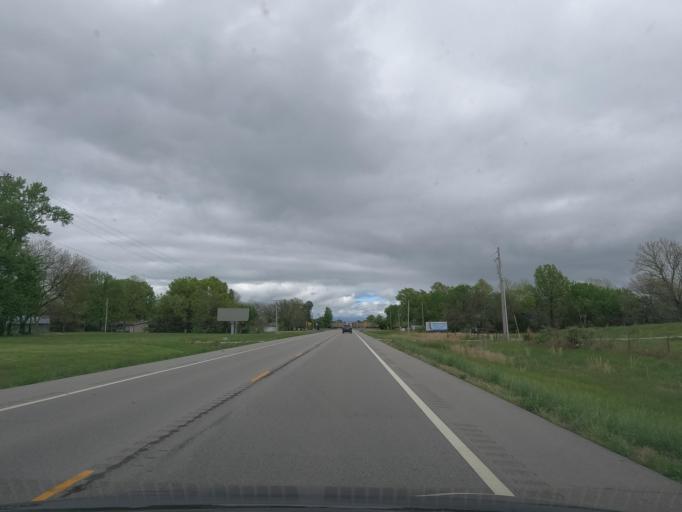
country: US
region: Kansas
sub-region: Crawford County
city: Pittsburg
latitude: 37.3394
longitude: -94.8249
